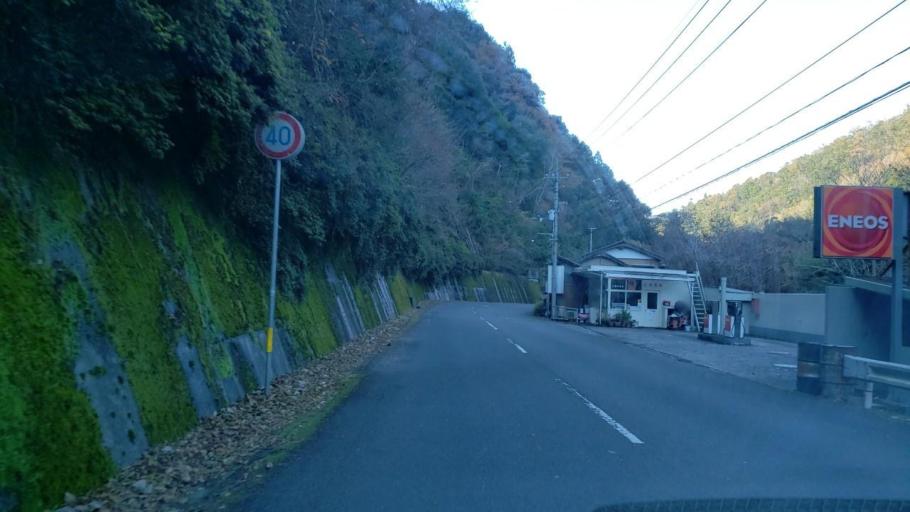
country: JP
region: Tokushima
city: Wakimachi
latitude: 34.0034
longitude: 134.0354
